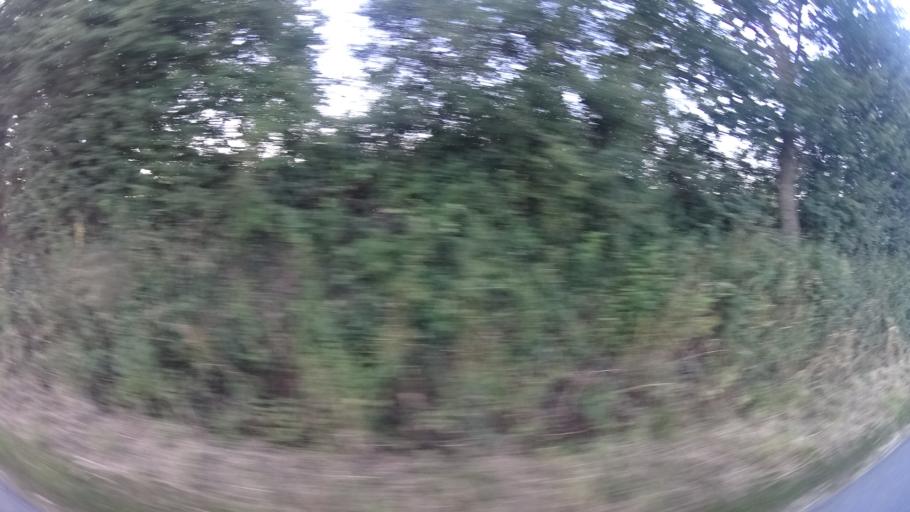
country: FR
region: Brittany
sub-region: Departement d'Ille-et-Vilaine
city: Grand-Fougeray
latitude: 47.7268
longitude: -1.7467
